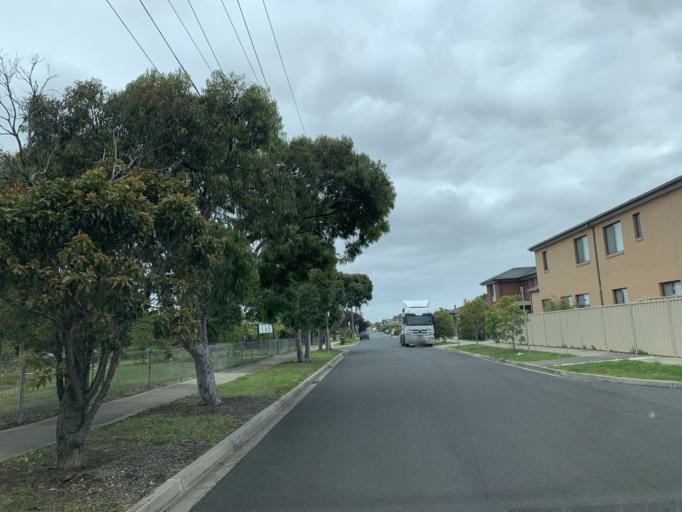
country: AU
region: Victoria
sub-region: Brimbank
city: St Albans
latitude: -37.7544
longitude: 144.8011
